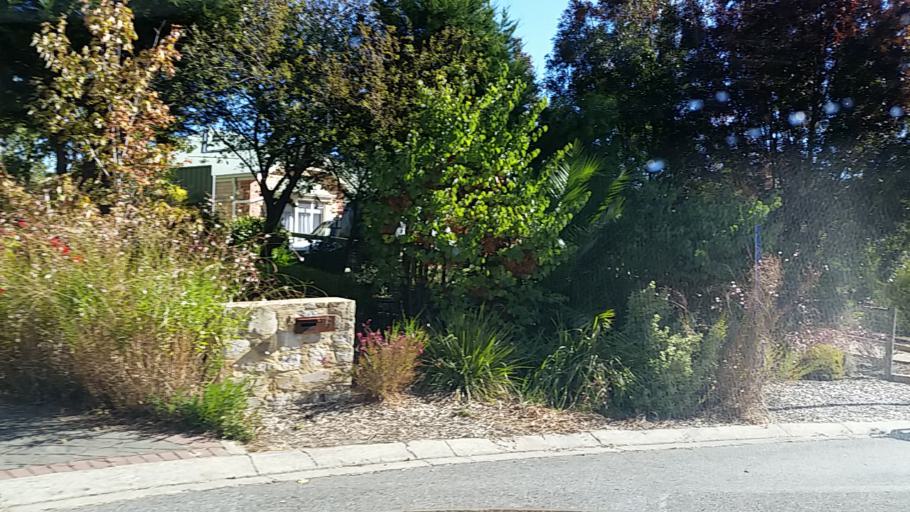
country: AU
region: South Australia
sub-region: Mount Barker
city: Mount Barker
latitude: -35.0637
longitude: 138.8781
